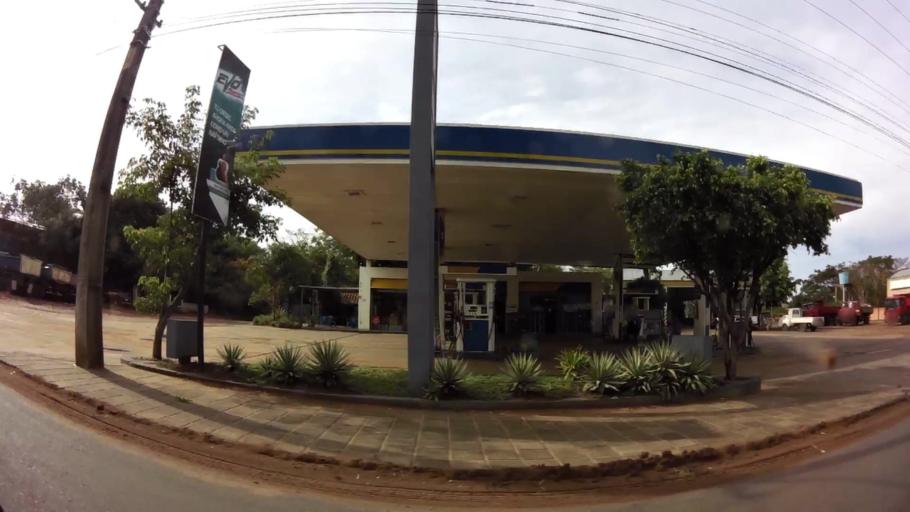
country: PY
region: Central
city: Limpio
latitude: -25.1667
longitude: -57.4697
